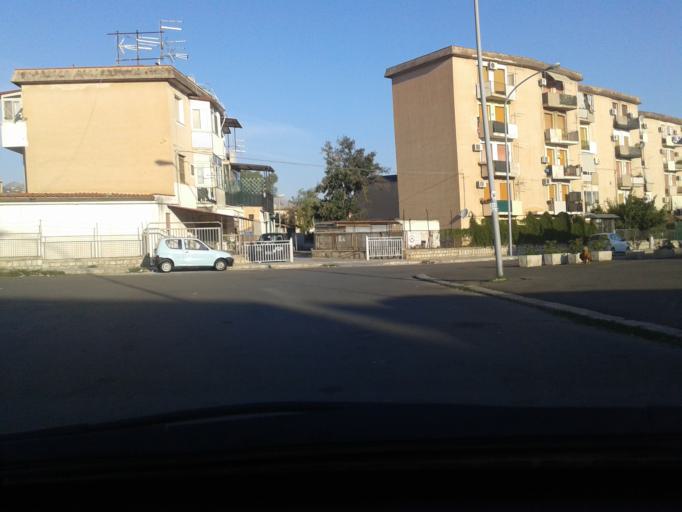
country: IT
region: Sicily
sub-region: Palermo
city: Villa Ciambra
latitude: 38.0886
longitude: 13.3546
